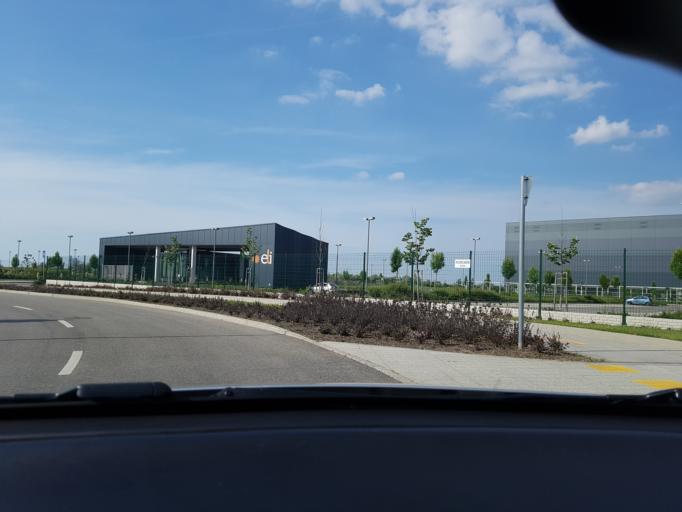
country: HU
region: Csongrad
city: Szeged
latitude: 46.2791
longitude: 20.1034
